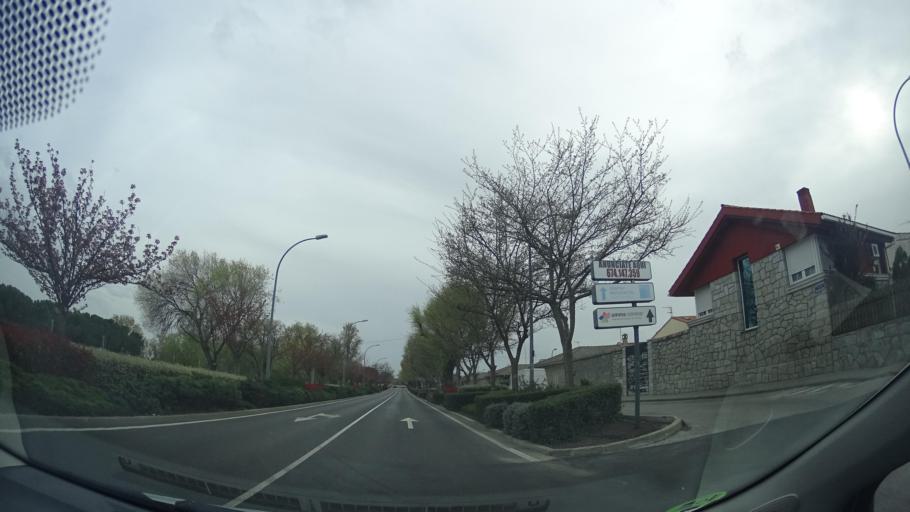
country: ES
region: Madrid
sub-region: Provincia de Madrid
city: Colmenar Viejo
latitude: 40.6695
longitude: -3.7699
